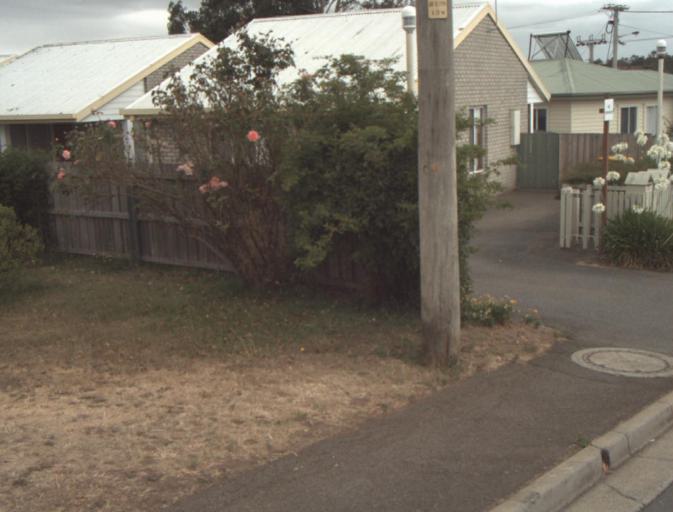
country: AU
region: Tasmania
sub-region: Launceston
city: Newstead
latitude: -41.4350
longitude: 147.1884
